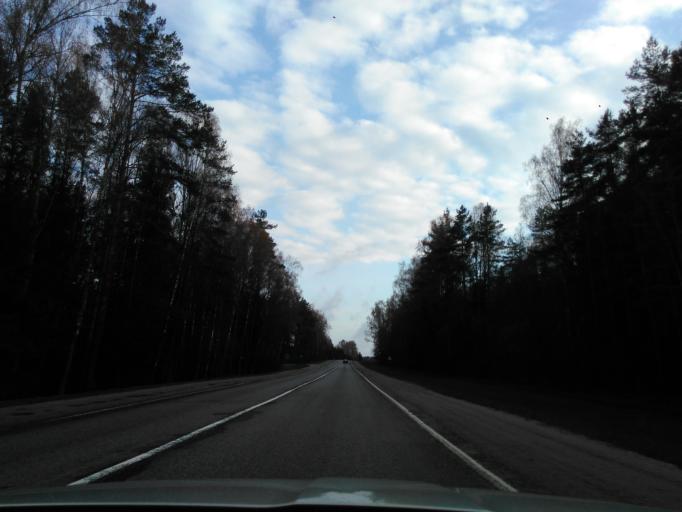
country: BY
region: Minsk
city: Lahoysk
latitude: 54.2970
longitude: 27.8741
